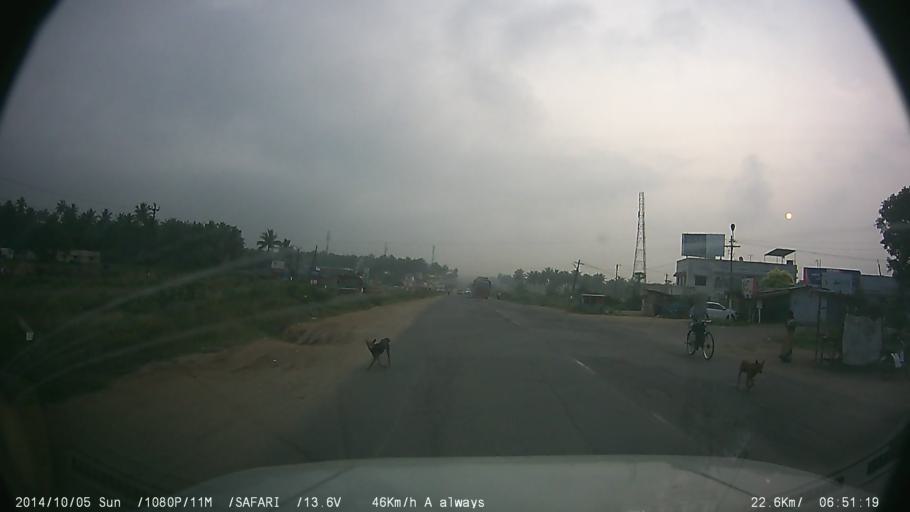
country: IN
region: Tamil Nadu
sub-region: Coimbatore
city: Madukkarai
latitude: 10.8624
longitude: 76.8730
